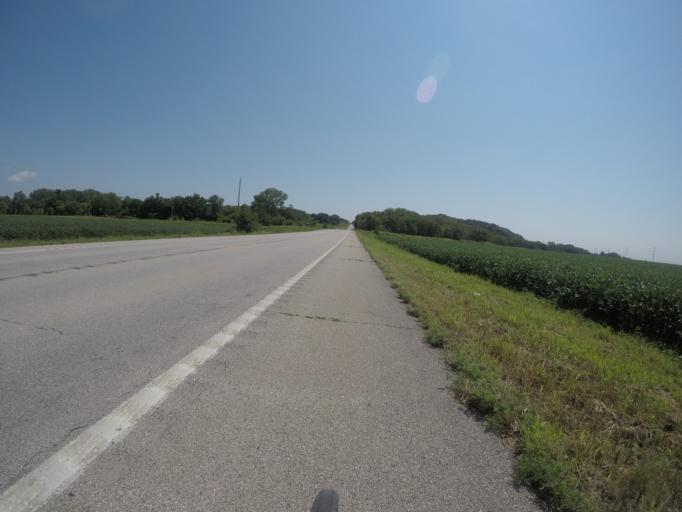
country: US
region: Missouri
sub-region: Platte County
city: Weston
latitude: 39.4375
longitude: -94.9343
